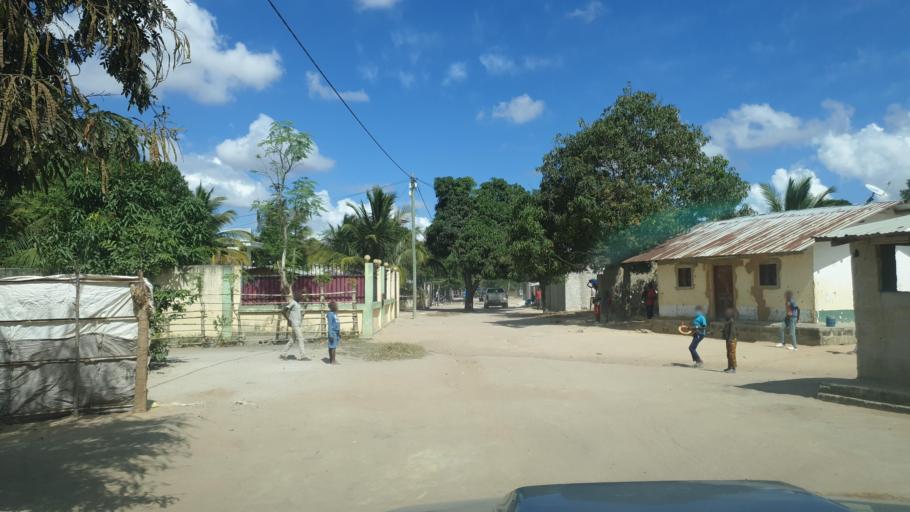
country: MZ
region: Nampula
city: Nacala
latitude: -14.5703
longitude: 40.6987
